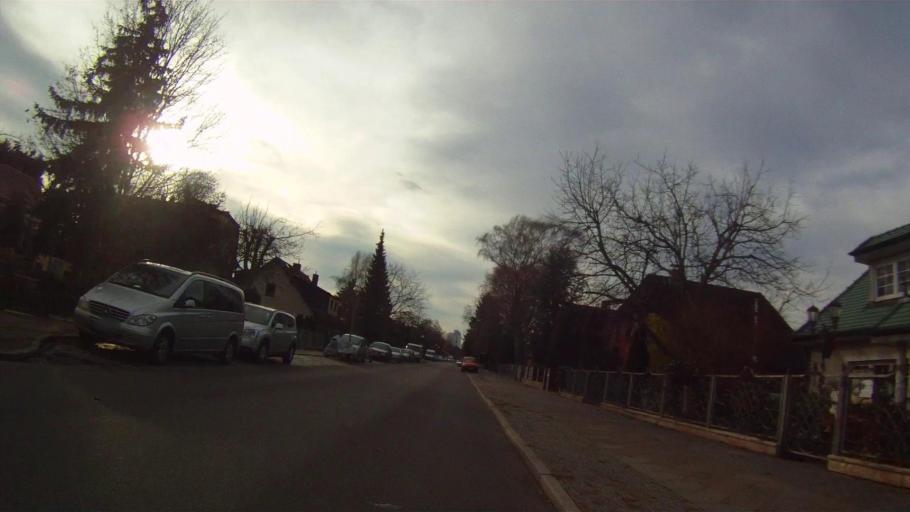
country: DE
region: Berlin
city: Rudow
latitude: 52.4342
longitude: 13.4869
